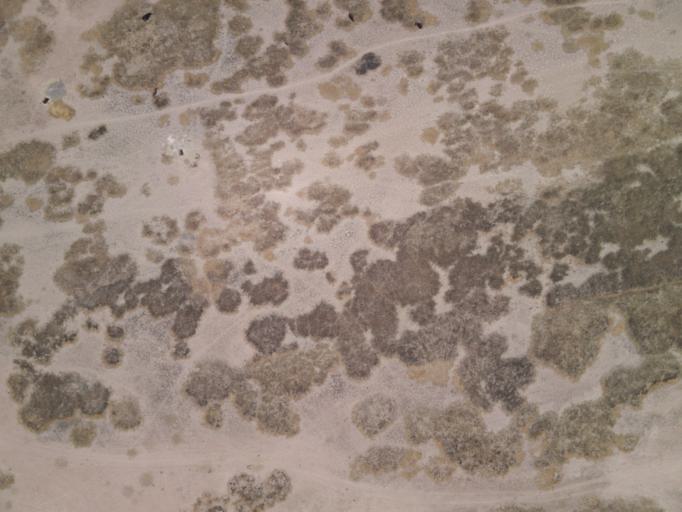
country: BO
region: La Paz
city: Batallas
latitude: -16.3572
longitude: -68.6288
